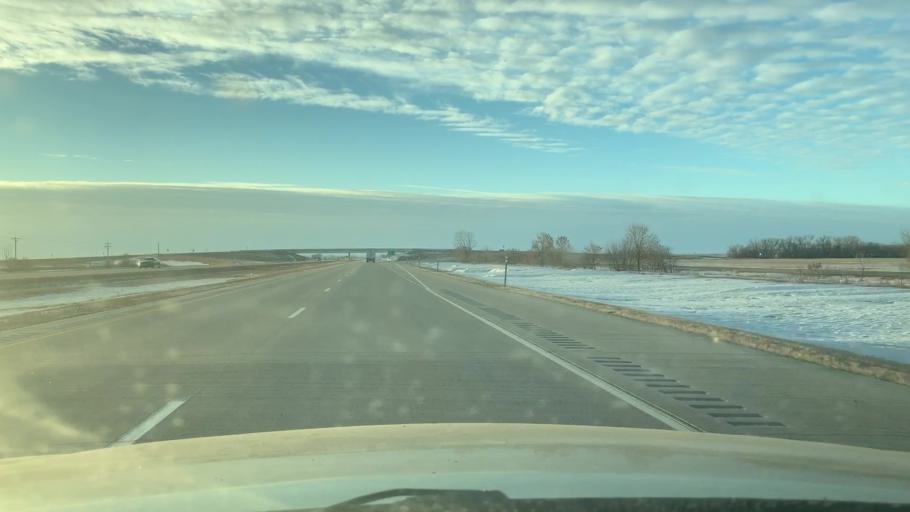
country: US
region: North Dakota
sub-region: Cass County
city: Casselton
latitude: 46.8758
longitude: -97.3385
